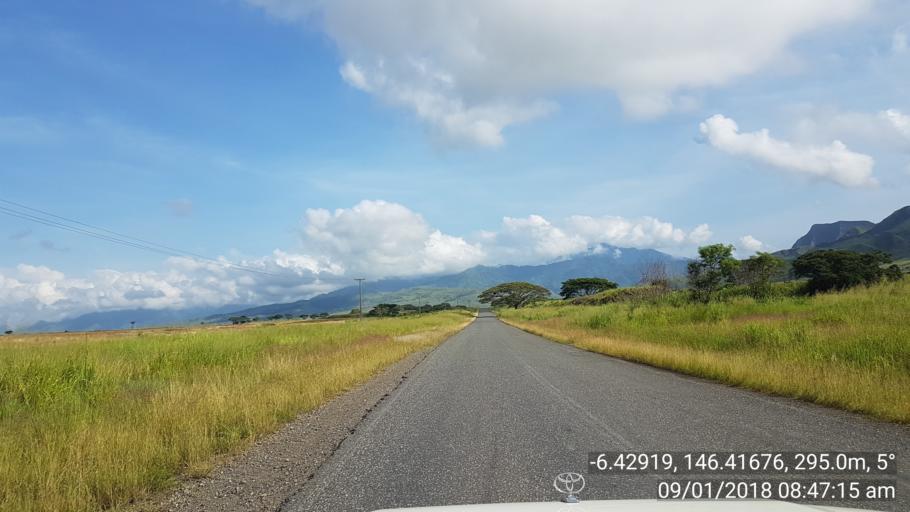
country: PG
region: Eastern Highlands
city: Kainantu
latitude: -6.4292
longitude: 146.4167
